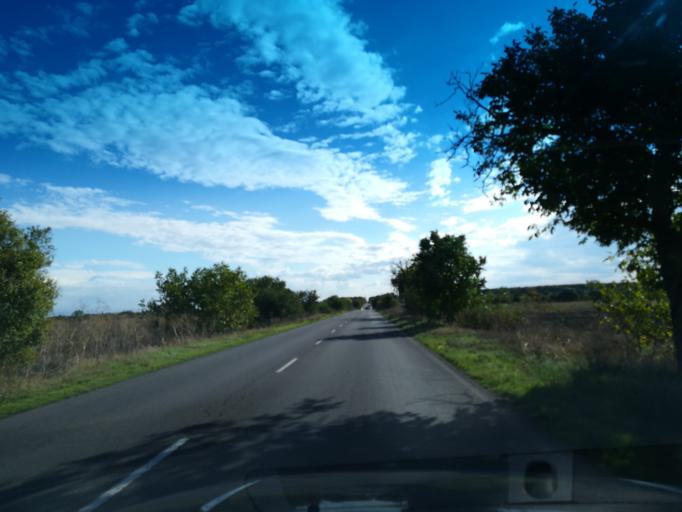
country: BG
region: Stara Zagora
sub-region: Obshtina Stara Zagora
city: Stara Zagora
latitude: 42.3653
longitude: 25.6546
